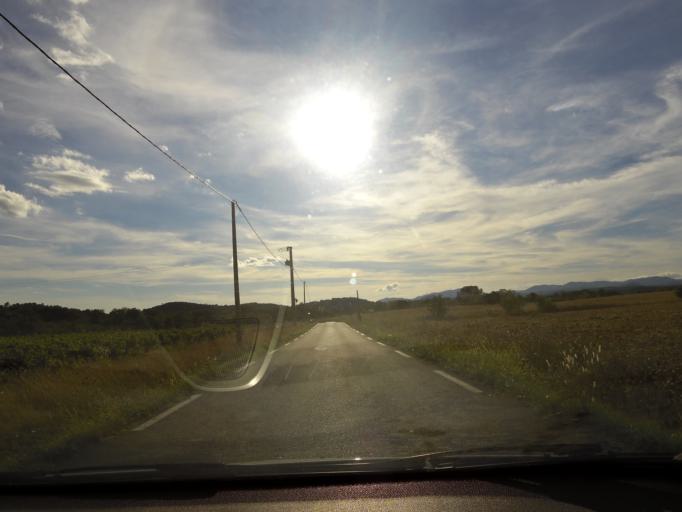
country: FR
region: Languedoc-Roussillon
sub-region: Departement du Gard
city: Quissac
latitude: 43.9551
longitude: 4.0116
